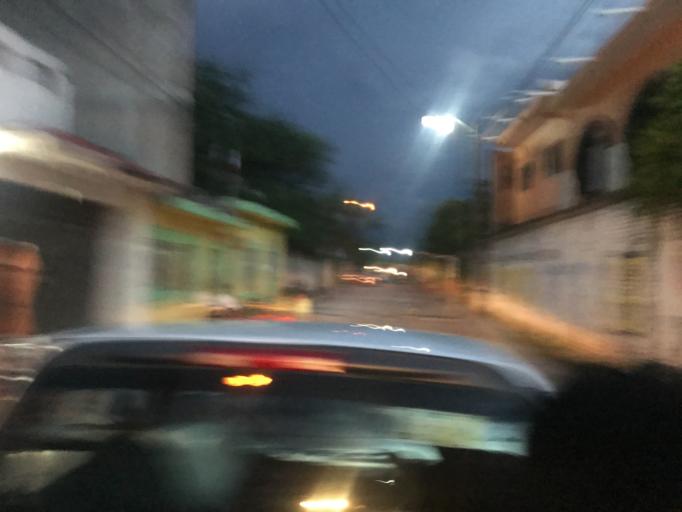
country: MX
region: Morelos
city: Axochiapan
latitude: 18.5048
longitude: -98.7597
